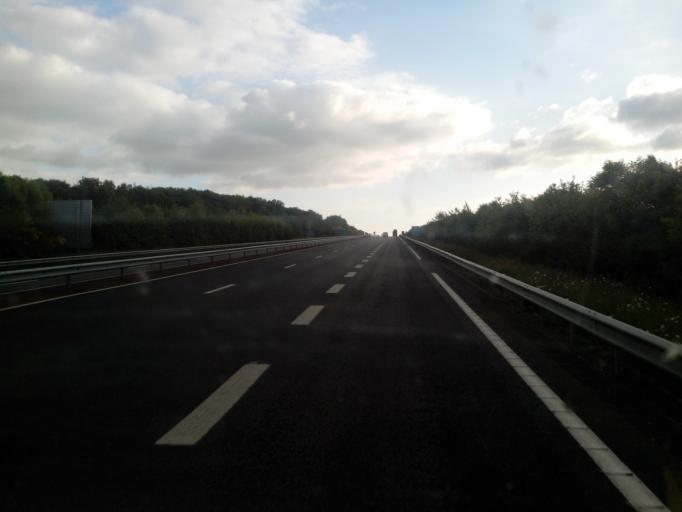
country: FR
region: Lower Normandy
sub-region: Departement de la Manche
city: Tessy-sur-Vire
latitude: 48.9193
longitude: -1.0860
